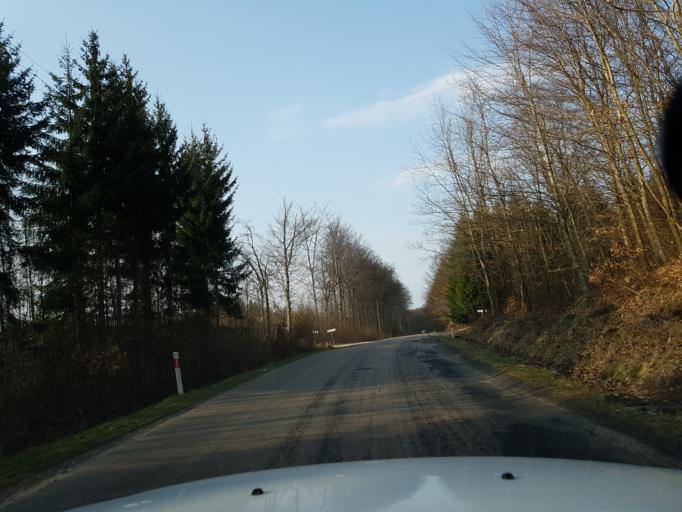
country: PL
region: West Pomeranian Voivodeship
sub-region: Powiat swidwinski
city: Polczyn-Zdroj
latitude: 53.7325
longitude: 16.0755
